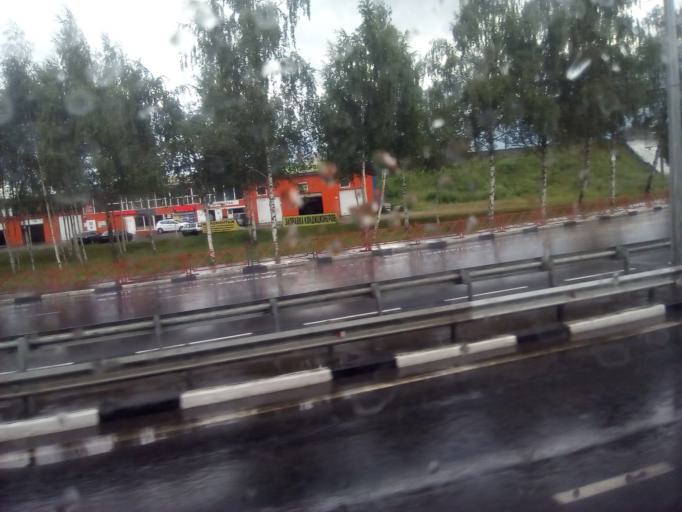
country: RU
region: Jaroslavl
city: Yaroslavl
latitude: 57.5973
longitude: 39.8942
